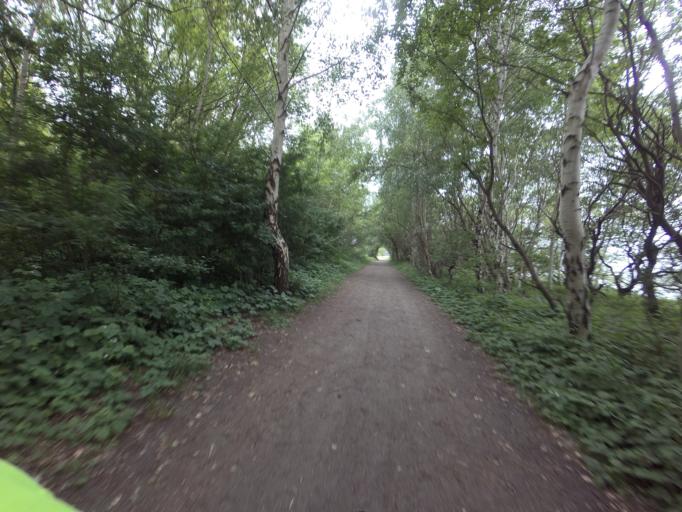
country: SE
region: Skane
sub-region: Malmo
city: Bunkeflostrand
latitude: 55.5255
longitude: 12.9056
